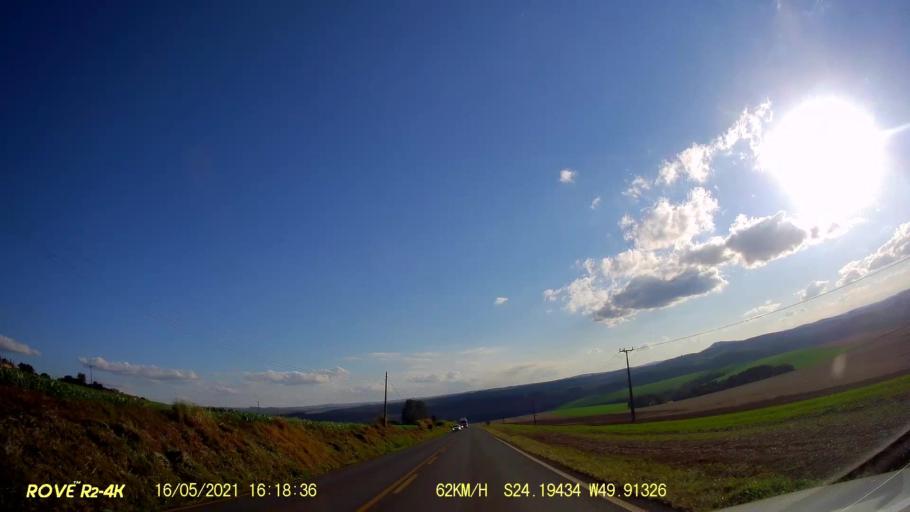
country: BR
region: Parana
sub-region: Jaguariaiva
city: Jaguariaiva
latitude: -24.1944
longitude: -49.9133
